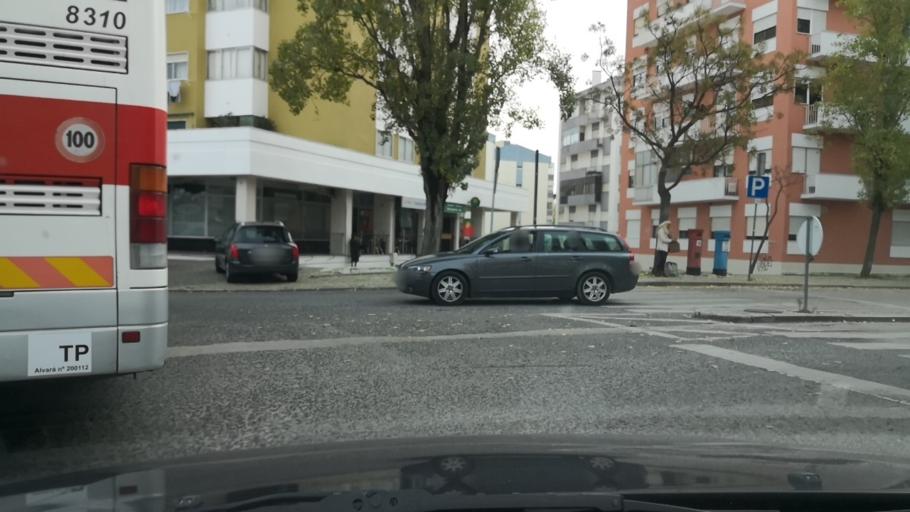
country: PT
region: Setubal
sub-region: Setubal
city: Setubal
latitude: 38.5340
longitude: -8.8683
